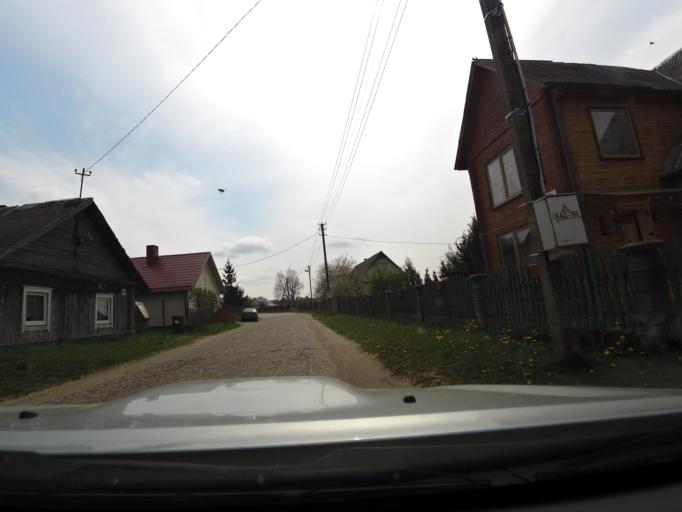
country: LT
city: Baltoji Voke
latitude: 54.4338
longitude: 25.1502
